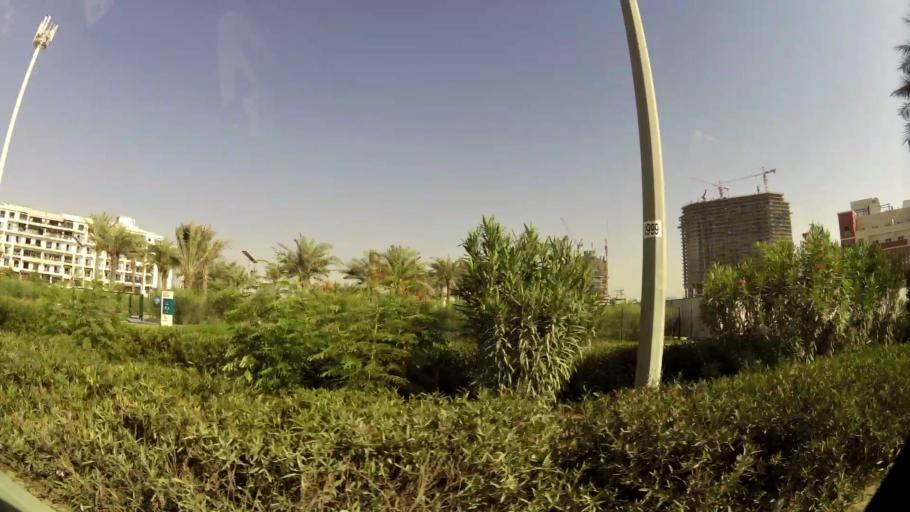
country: AE
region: Dubai
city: Dubai
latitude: 25.0607
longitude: 55.2061
